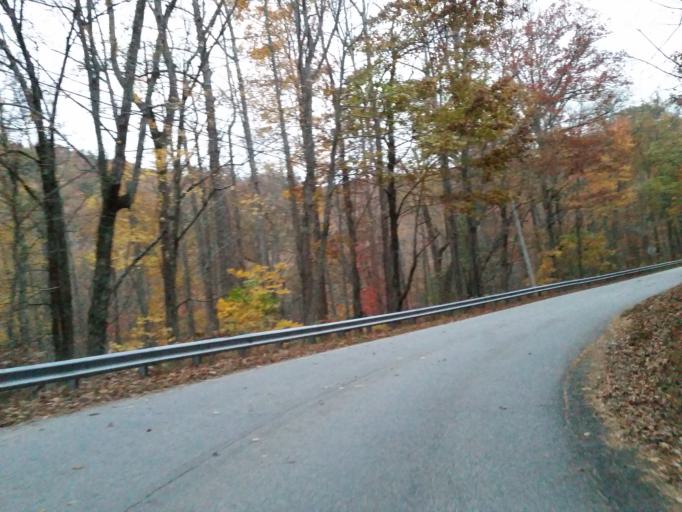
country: US
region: Georgia
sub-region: Lumpkin County
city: Dahlonega
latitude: 34.7011
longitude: -84.0316
